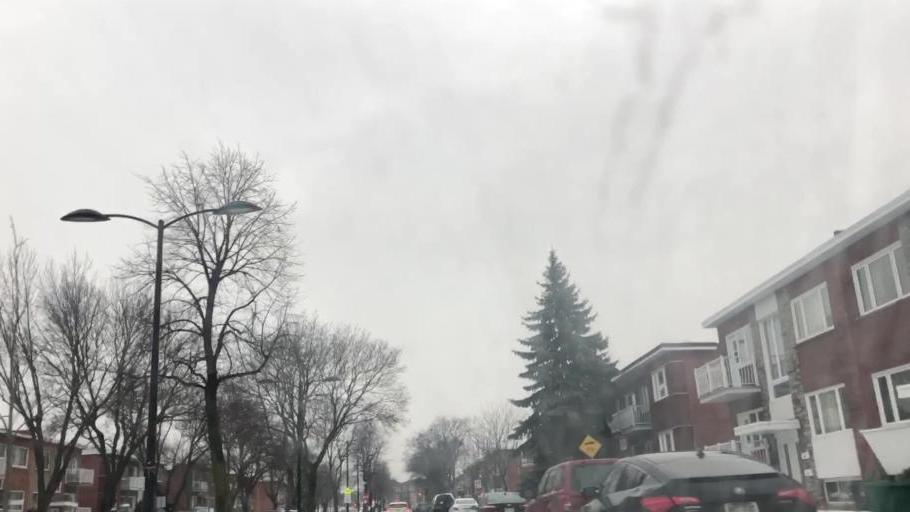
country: CA
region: Quebec
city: Saint-Laurent
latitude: 45.5157
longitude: -73.7233
